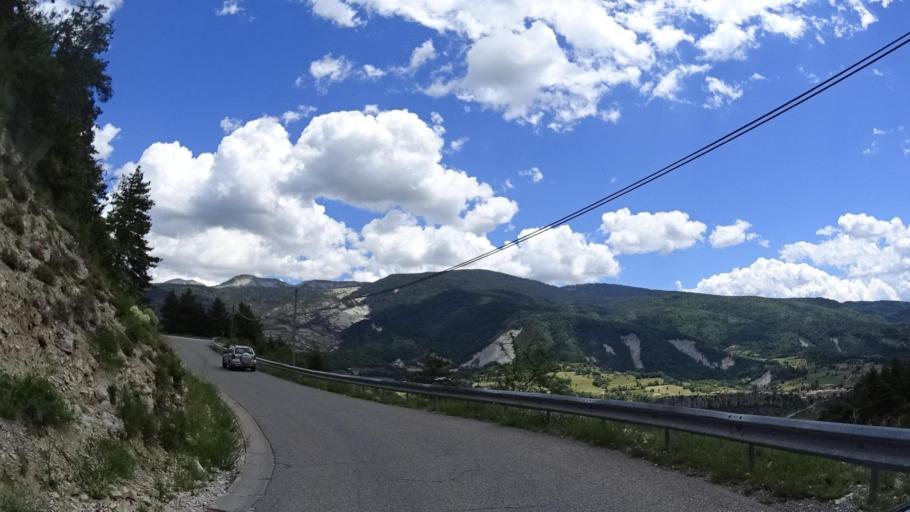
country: FR
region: Provence-Alpes-Cote d'Azur
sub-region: Departement des Alpes-de-Haute-Provence
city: Annot
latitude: 44.0253
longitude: 6.6161
